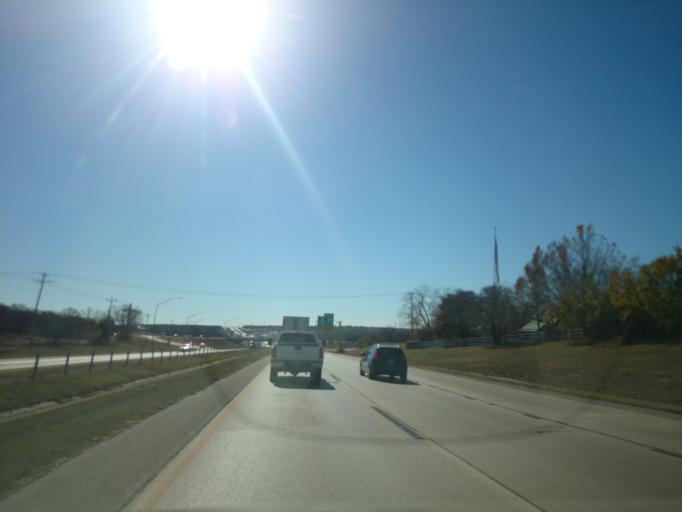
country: US
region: Oklahoma
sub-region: Oklahoma County
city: Edmond
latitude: 35.6568
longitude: -97.4237
